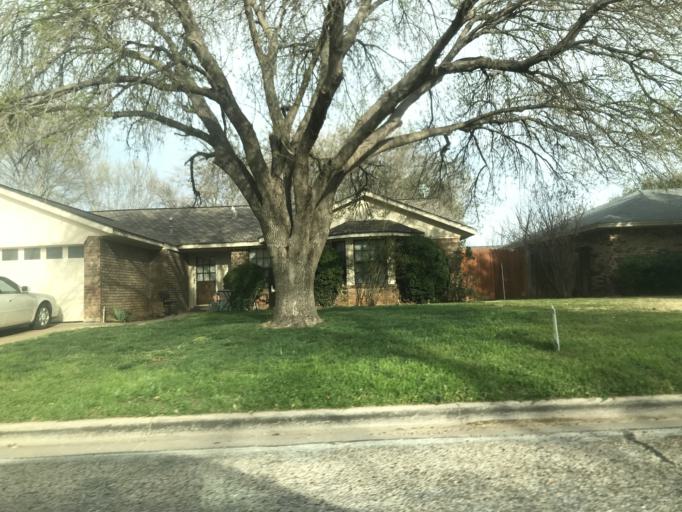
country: US
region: Texas
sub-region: Taylor County
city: Abilene
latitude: 32.3961
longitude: -99.7705
